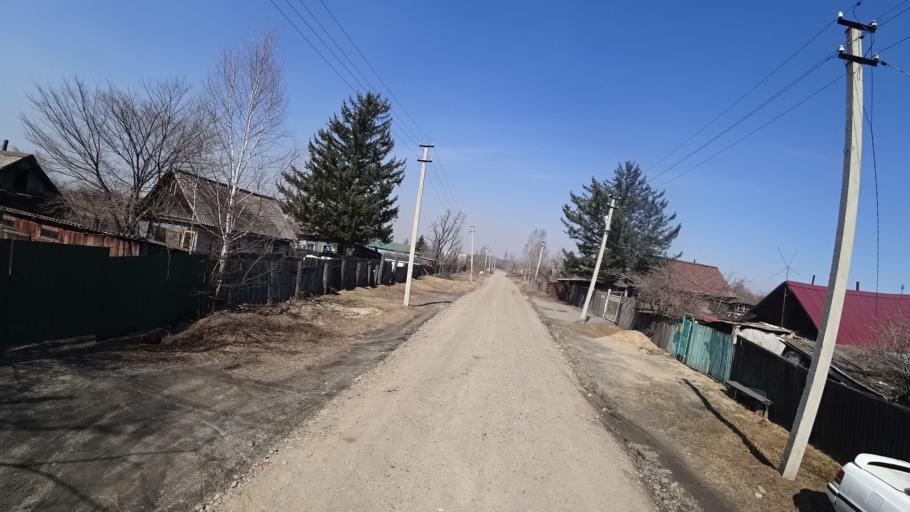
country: RU
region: Amur
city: Novobureyskiy
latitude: 49.7891
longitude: 129.8539
